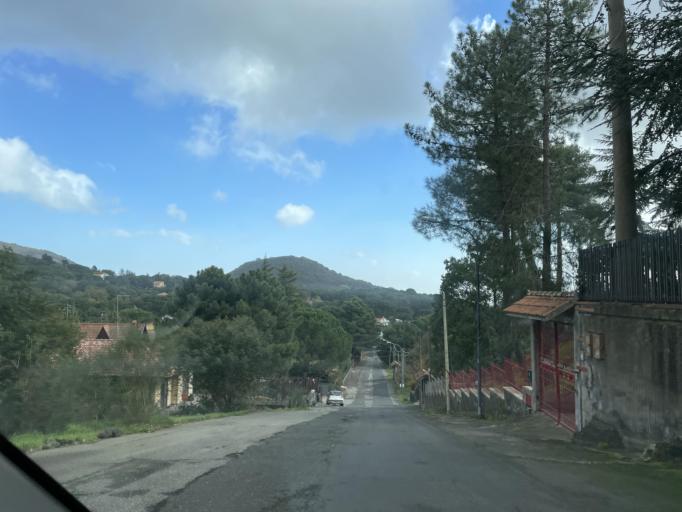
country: IT
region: Sicily
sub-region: Catania
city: Nicolosi
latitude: 37.6291
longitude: 15.0185
